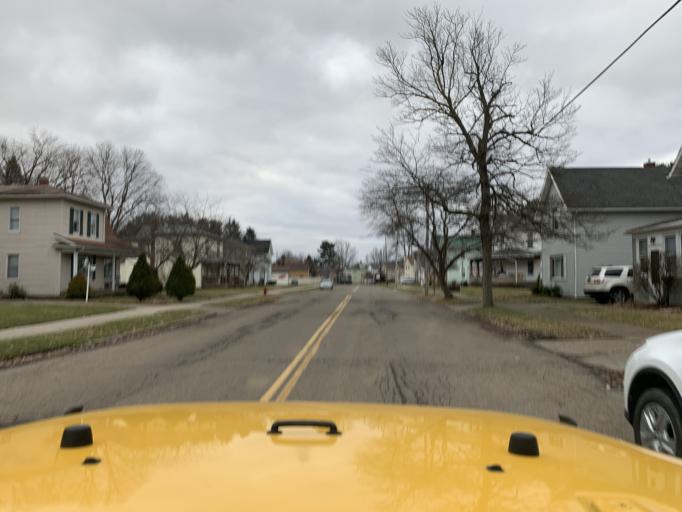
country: US
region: Ohio
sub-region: Tuscarawas County
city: Dover
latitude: 40.5265
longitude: -81.4783
